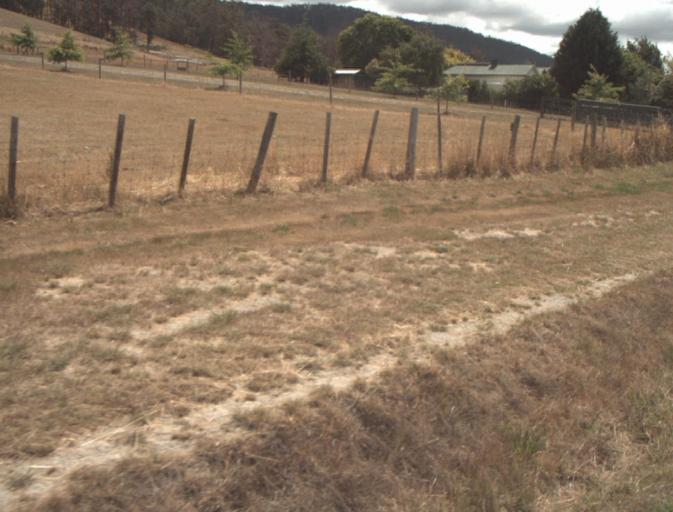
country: AU
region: Tasmania
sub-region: Launceston
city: Mayfield
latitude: -41.2393
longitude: 147.1355
